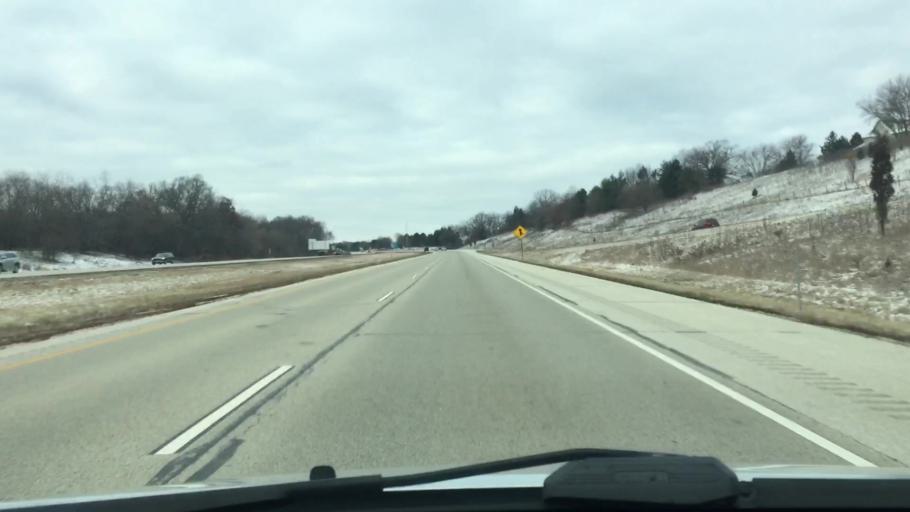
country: US
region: Wisconsin
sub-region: Waukesha County
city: Hartland
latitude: 43.1057
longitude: -88.3152
